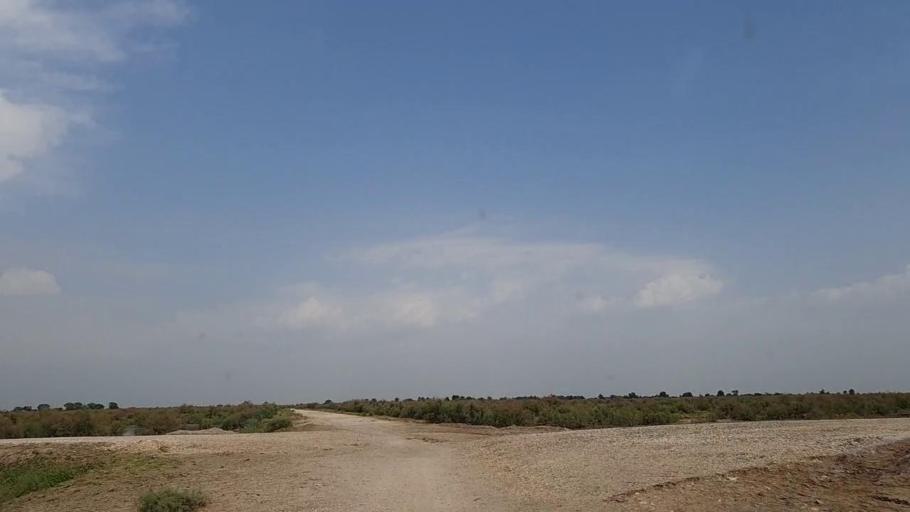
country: PK
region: Sindh
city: Khanpur
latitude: 27.8306
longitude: 69.5078
